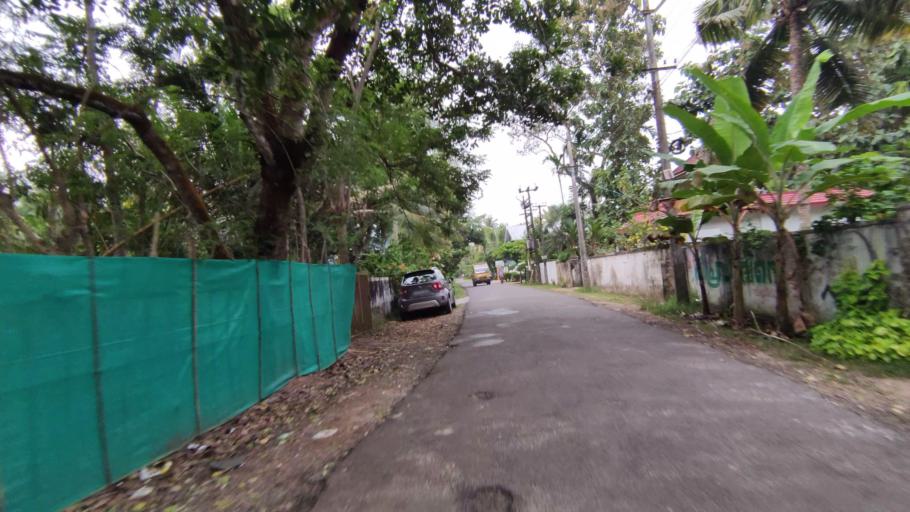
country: IN
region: Kerala
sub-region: Alappuzha
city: Shertallai
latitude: 9.6084
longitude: 76.3531
